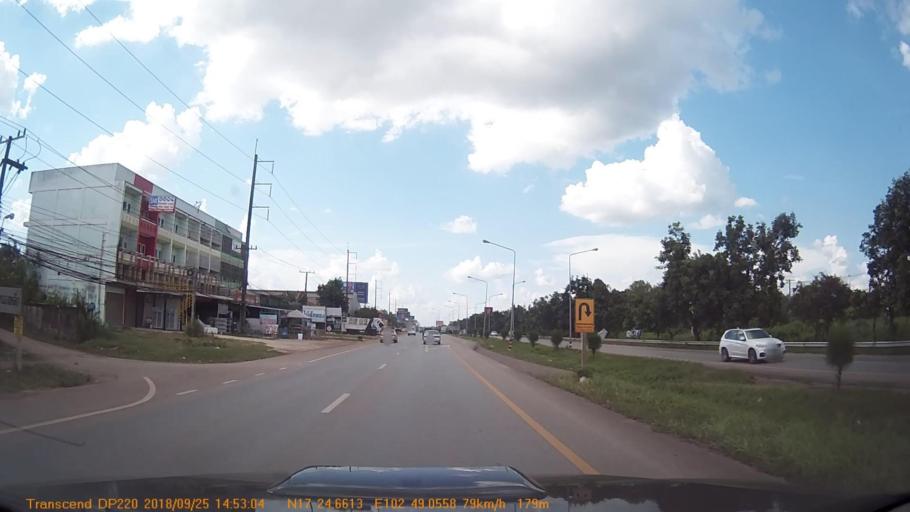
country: TH
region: Changwat Udon Thani
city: Udon Thani
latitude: 17.4115
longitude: 102.8174
